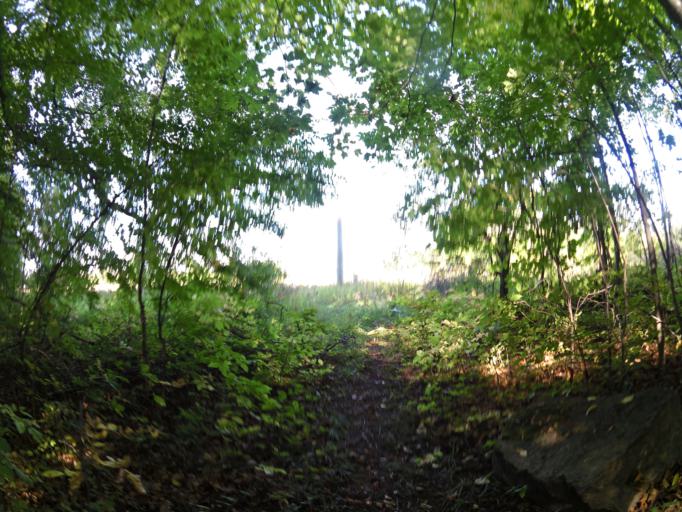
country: CA
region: Ontario
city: Bells Corners
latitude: 45.3386
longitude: -75.9256
